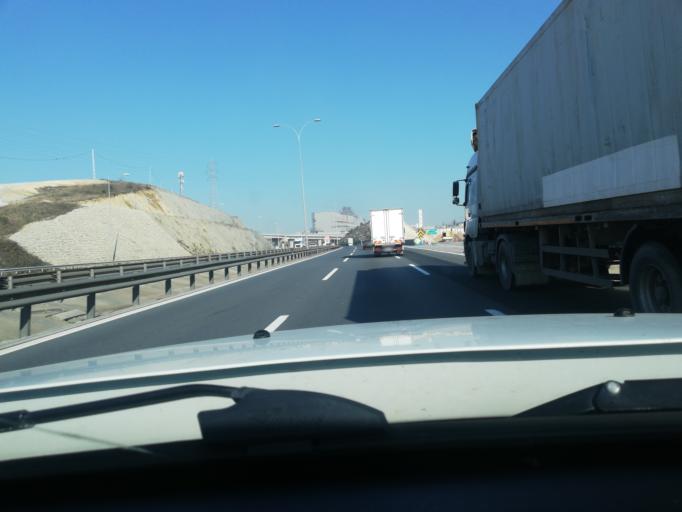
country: TR
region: Kocaeli
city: Tavsanli
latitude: 40.7934
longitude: 29.5154
